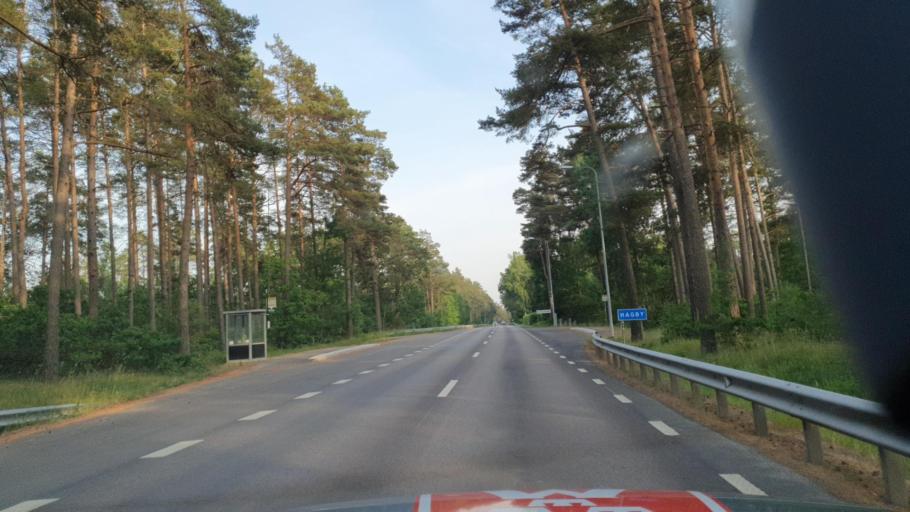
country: SE
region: Kalmar
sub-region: Kalmar Kommun
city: Ljungbyholm
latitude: 56.5797
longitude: 16.1758
